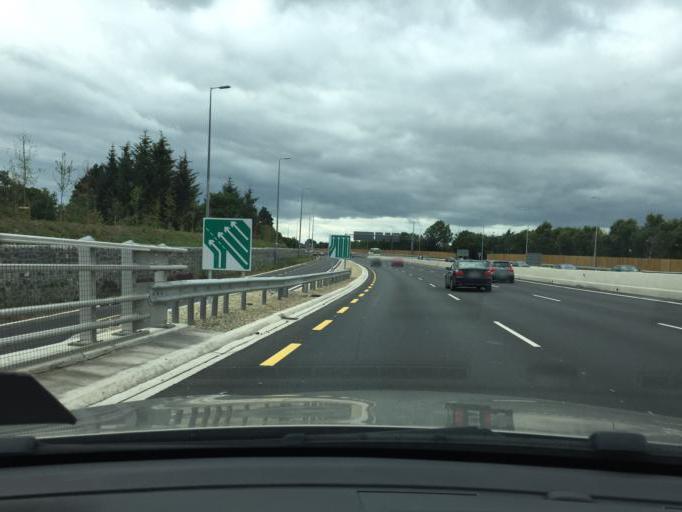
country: IE
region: Leinster
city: Clondalkin
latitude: 53.3122
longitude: -6.3944
